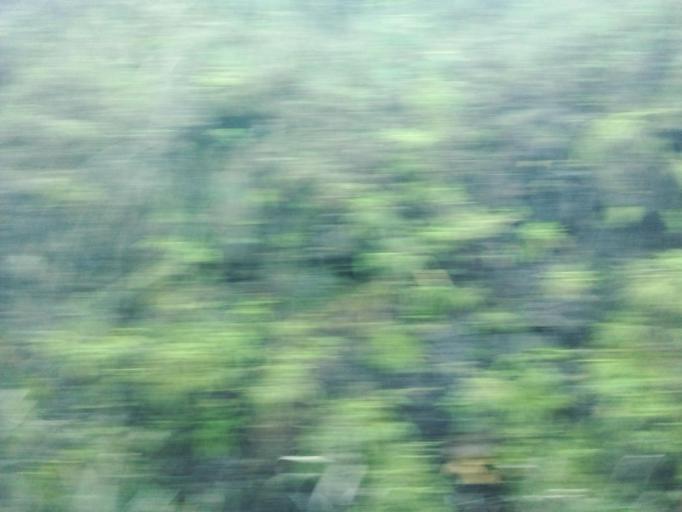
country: BR
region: Minas Gerais
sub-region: Rio Piracicaba
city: Rio Piracicaba
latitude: -19.8915
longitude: -43.1403
